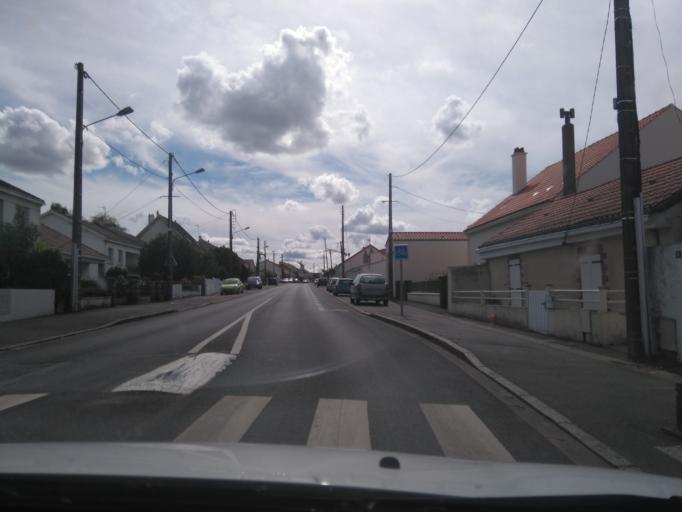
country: FR
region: Pays de la Loire
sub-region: Departement de la Loire-Atlantique
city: Reze
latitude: 47.1789
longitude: -1.5596
